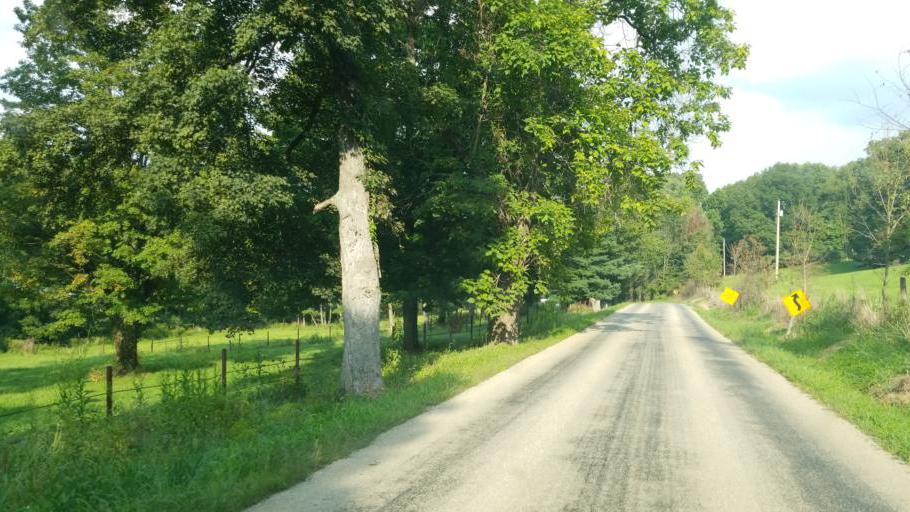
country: US
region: Ohio
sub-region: Knox County
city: Gambier
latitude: 40.3712
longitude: -82.4225
